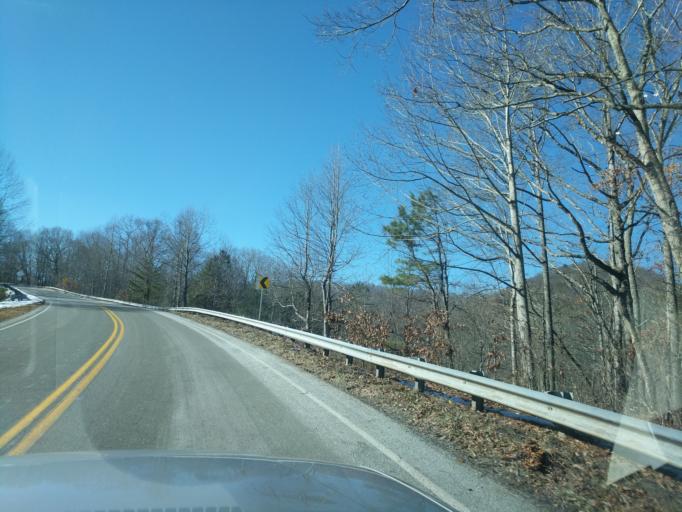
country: US
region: Georgia
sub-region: Rabun County
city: Clayton
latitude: 34.8752
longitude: -83.5674
